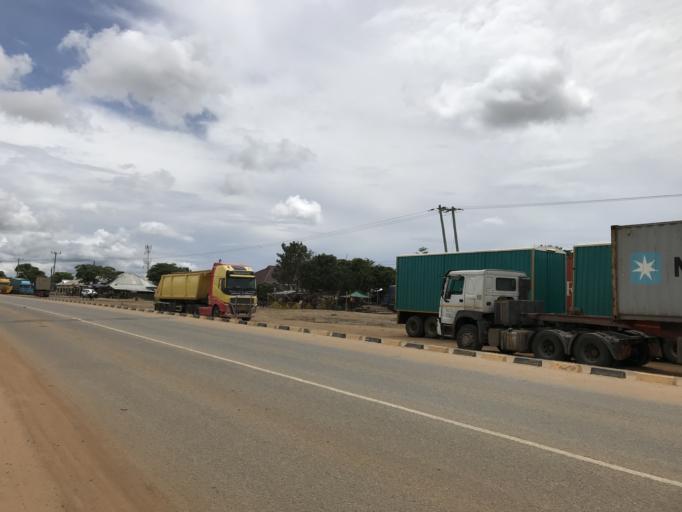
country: TZ
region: Singida
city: Kilimatinde
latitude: -5.7558
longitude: 34.8249
